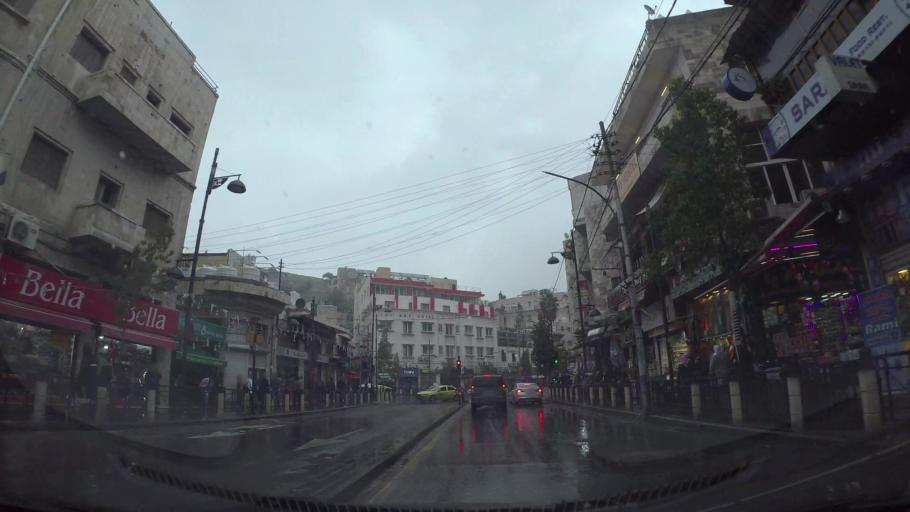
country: JO
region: Amman
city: Amman
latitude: 31.9522
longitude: 35.9317
